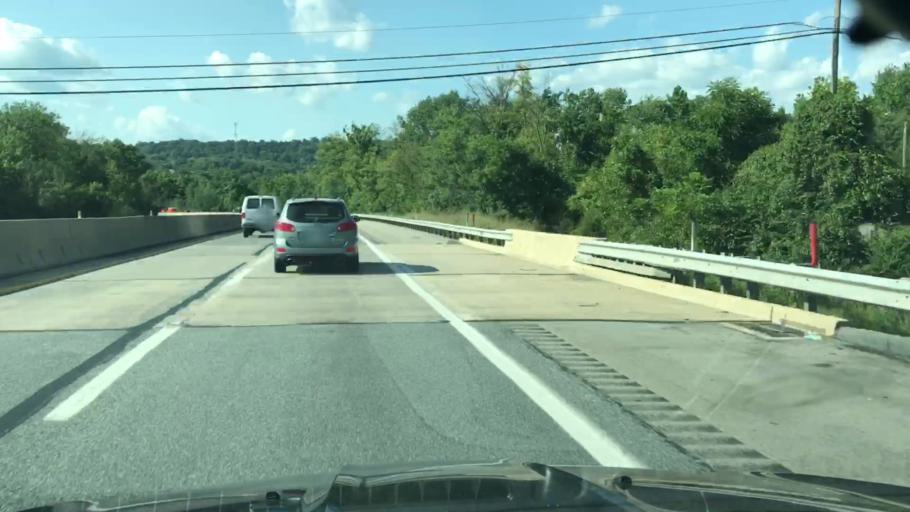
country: US
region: Pennsylvania
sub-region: Lancaster County
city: Denver
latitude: 40.2355
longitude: -76.1292
